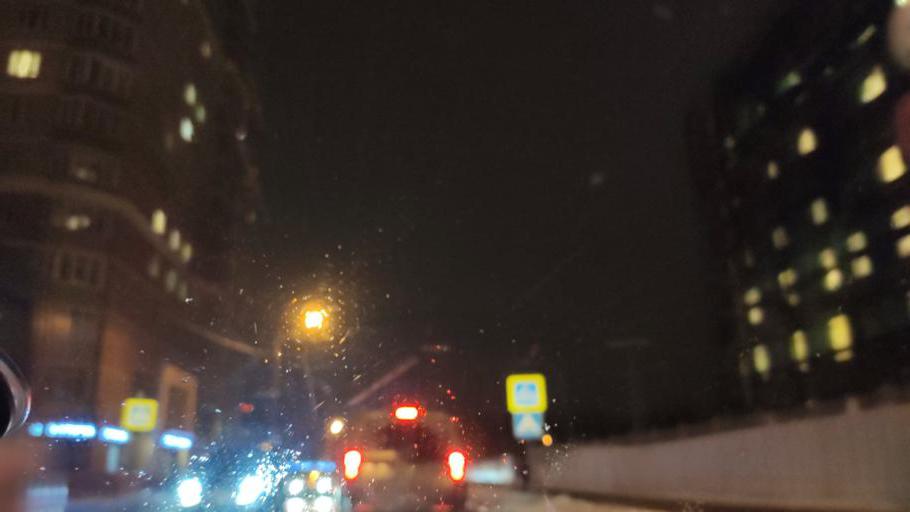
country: RU
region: Moskovskaya
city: Odintsovo
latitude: 55.6861
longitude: 37.2603
